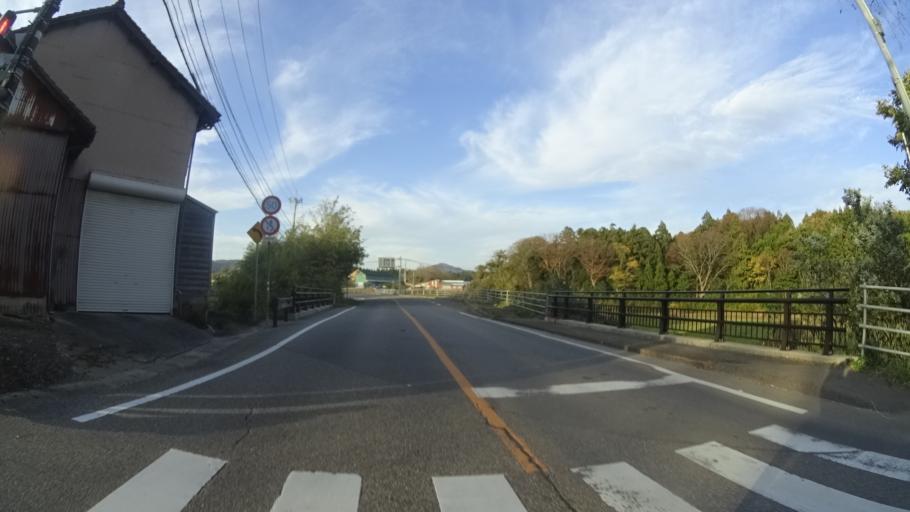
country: JP
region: Ishikawa
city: Nanao
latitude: 37.1547
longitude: 136.7206
